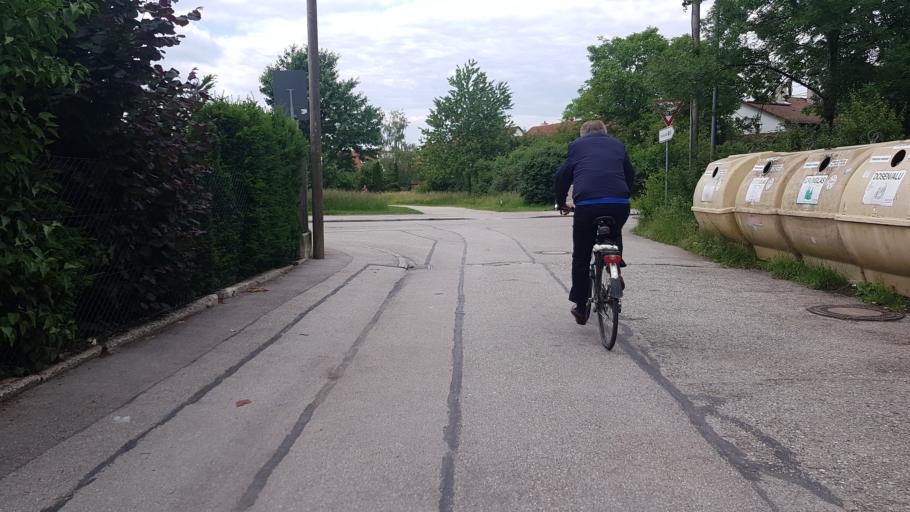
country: DE
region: Bavaria
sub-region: Upper Bavaria
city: Pasing
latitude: 48.1572
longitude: 11.4286
